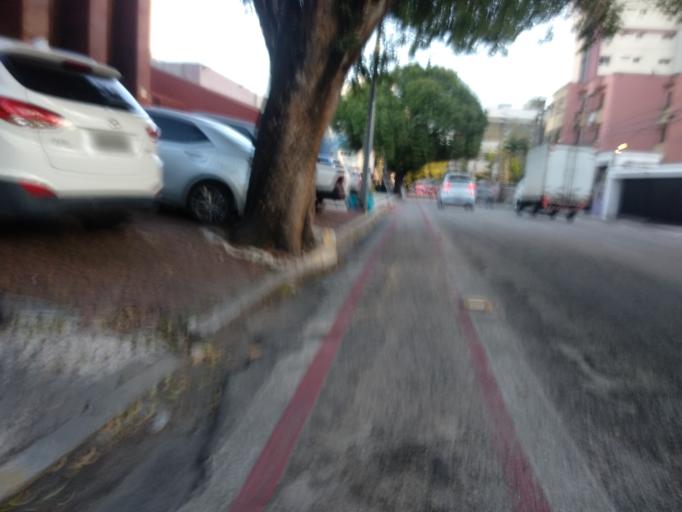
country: BR
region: Ceara
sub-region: Fortaleza
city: Fortaleza
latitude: -3.7352
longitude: -38.5091
